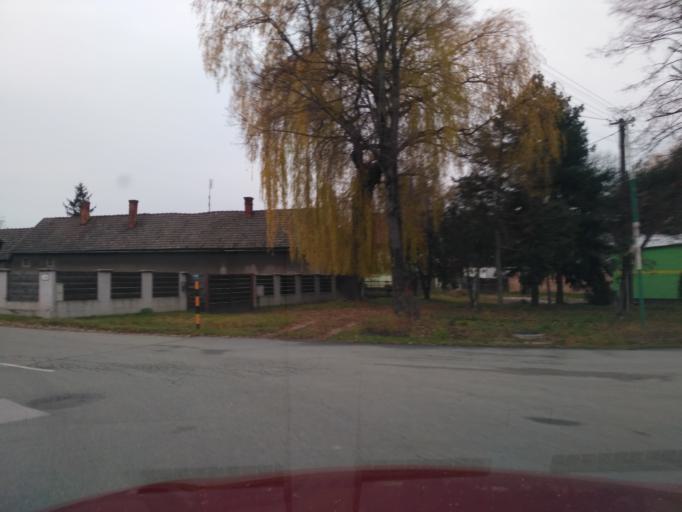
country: SK
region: Kosicky
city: Kosice
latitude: 48.5931
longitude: 21.1677
